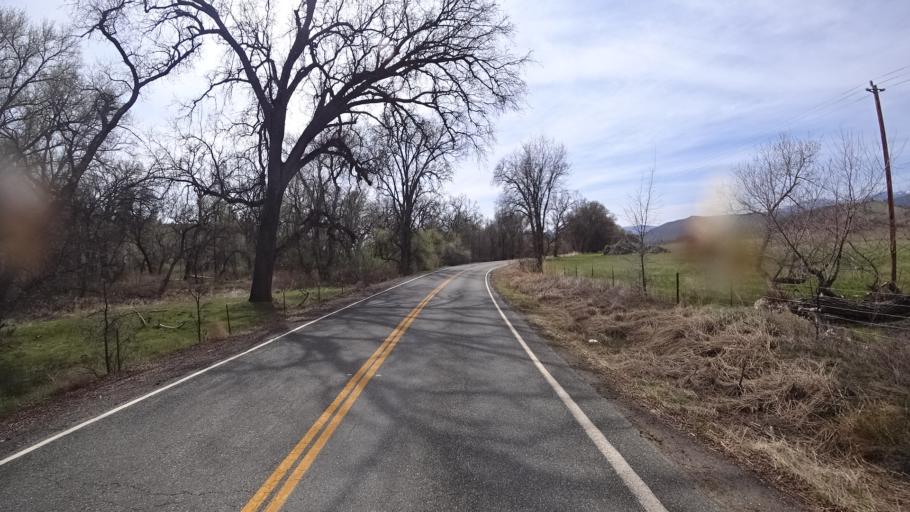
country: US
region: California
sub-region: Glenn County
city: Willows
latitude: 39.4182
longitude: -122.5375
